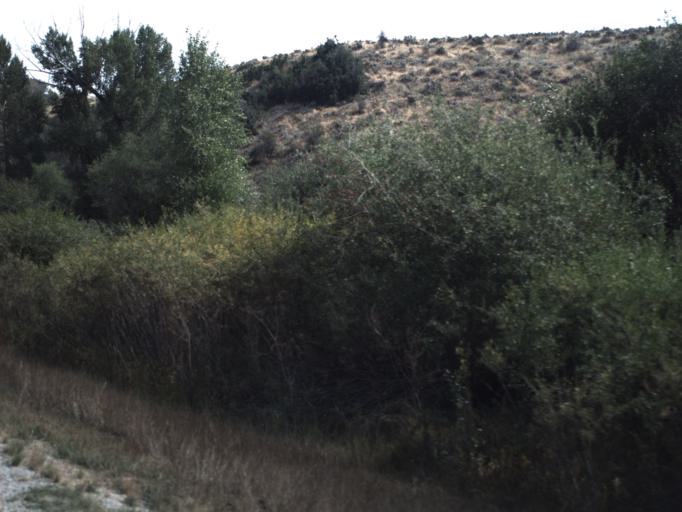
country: US
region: Utah
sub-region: Summit County
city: Summit Park
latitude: 40.8629
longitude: -111.5866
